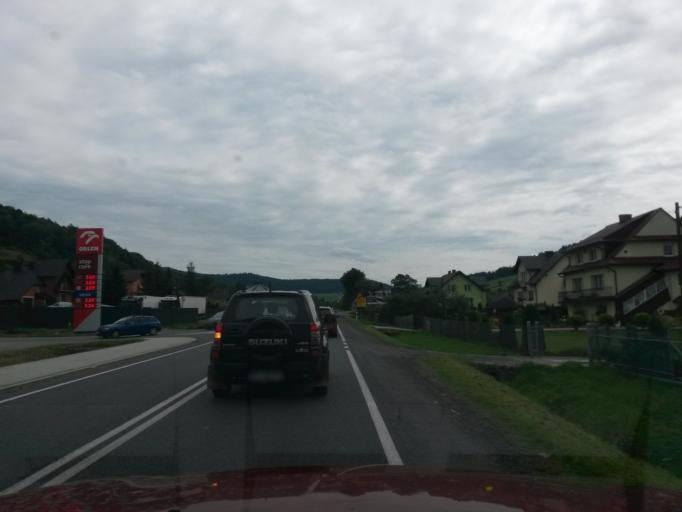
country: PL
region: Lesser Poland Voivodeship
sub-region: Powiat nowosadecki
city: Labowa
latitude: 49.5055
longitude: 20.8939
